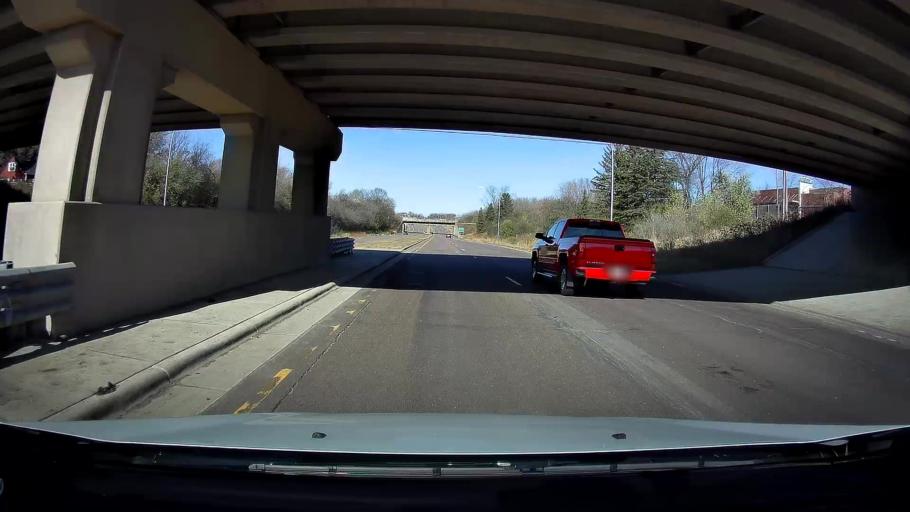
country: US
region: Minnesota
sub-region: Ramsey County
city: Arden Hills
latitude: 45.0500
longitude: -93.1567
